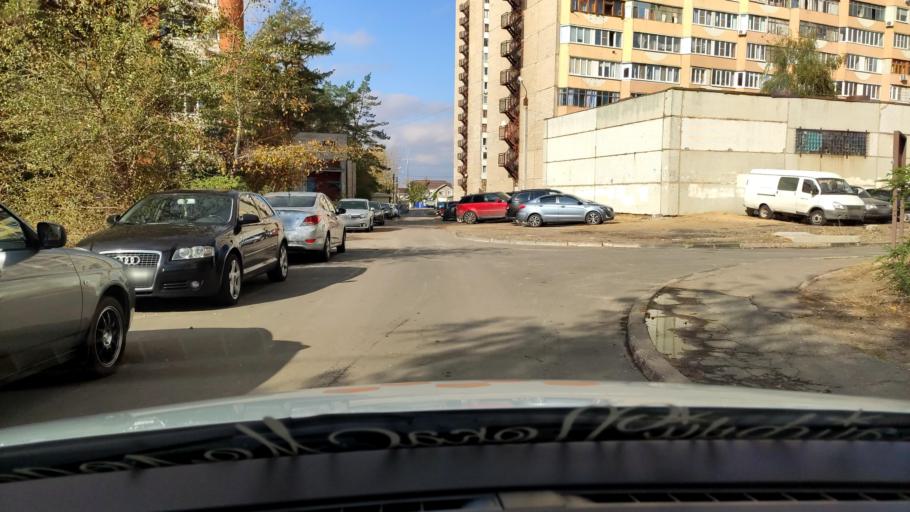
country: RU
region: Voronezj
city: Pridonskoy
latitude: 51.6862
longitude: 39.0816
